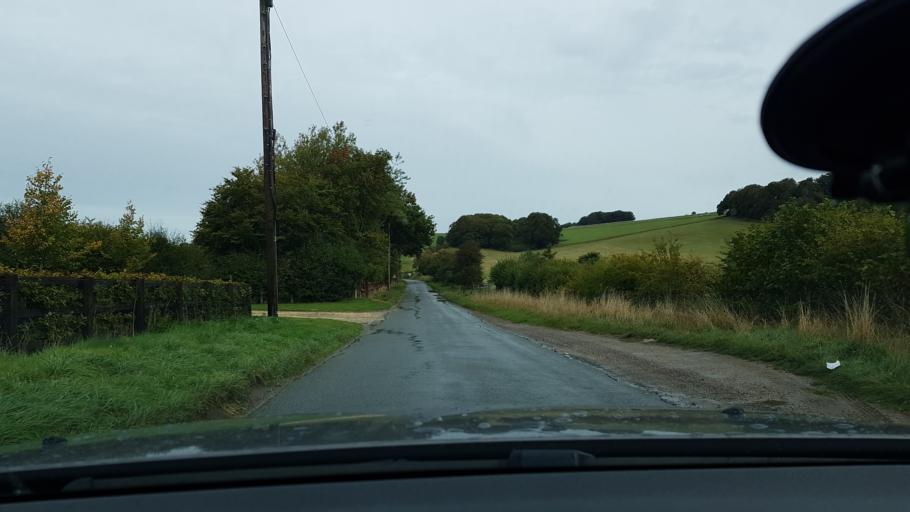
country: GB
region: England
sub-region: West Berkshire
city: Lambourn
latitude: 51.5404
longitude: -1.5282
